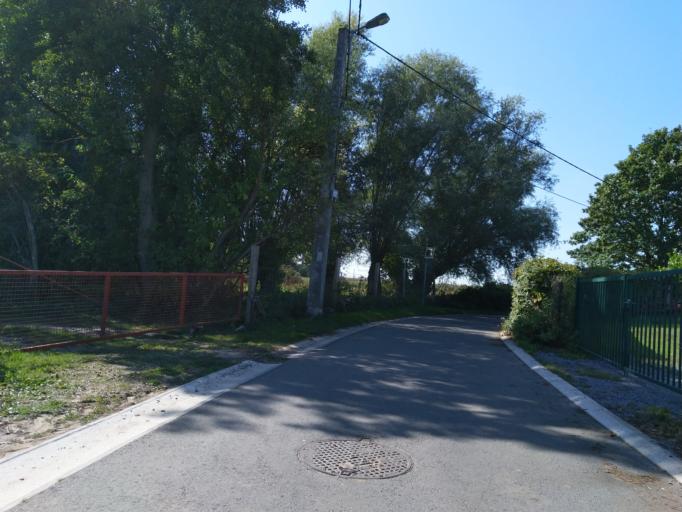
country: BE
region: Wallonia
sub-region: Province du Hainaut
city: Jurbise
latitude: 50.5290
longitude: 3.8813
